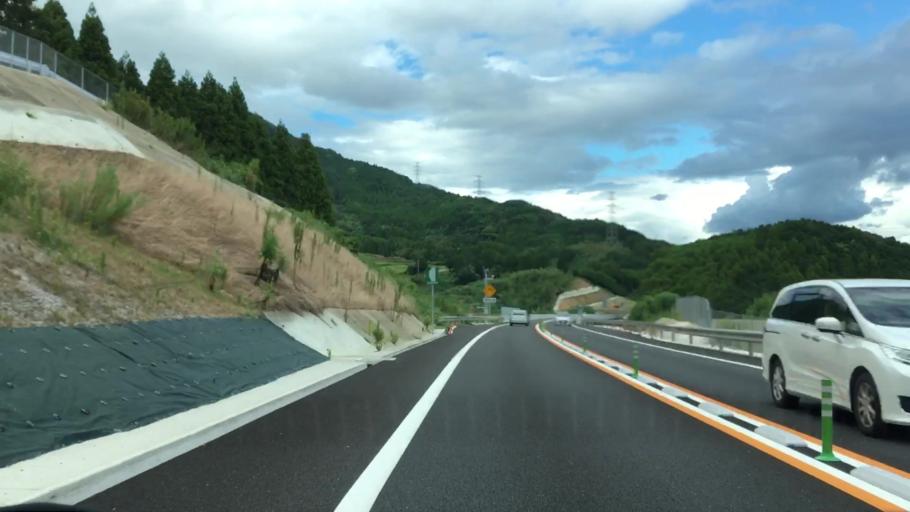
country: JP
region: Saga Prefecture
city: Imaricho-ko
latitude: 33.3098
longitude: 129.9168
